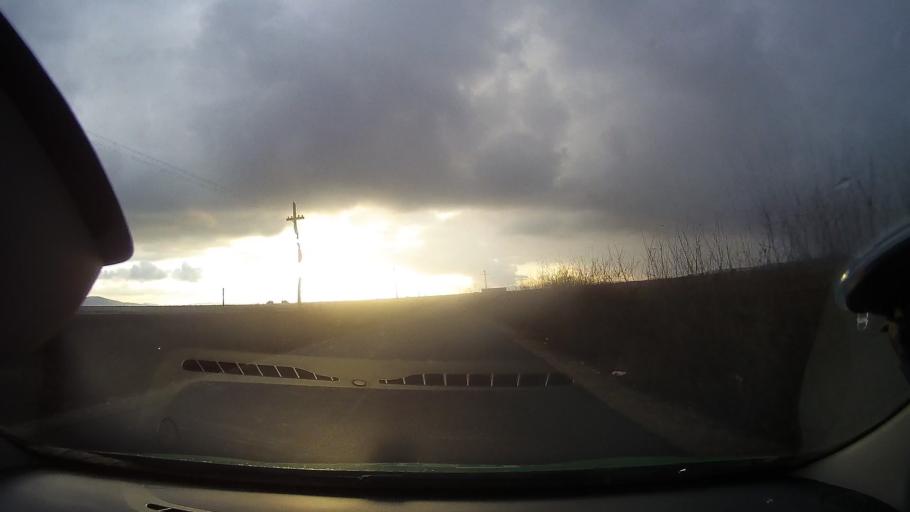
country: RO
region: Cluj
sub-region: Comuna Luna
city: Luncani
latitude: 46.4541
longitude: 23.9605
